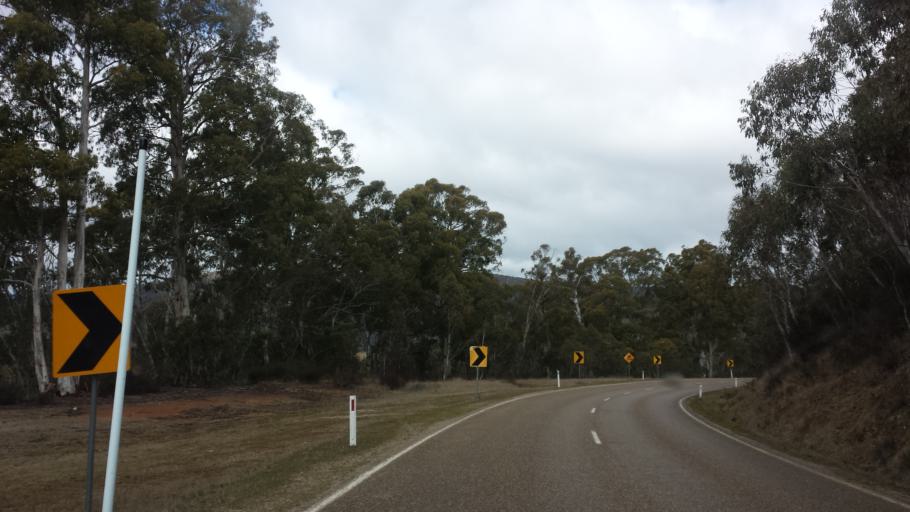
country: AU
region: Victoria
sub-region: Alpine
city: Mount Beauty
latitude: -37.0882
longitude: 147.3844
